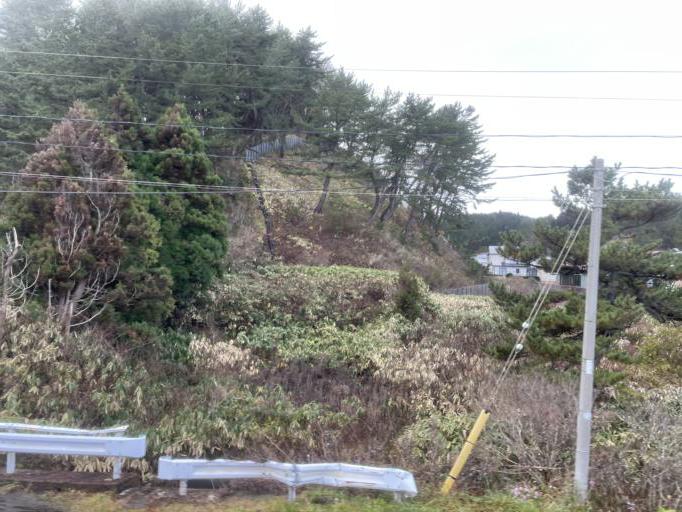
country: JP
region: Aomori
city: Aomori Shi
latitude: 41.0323
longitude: 140.6460
